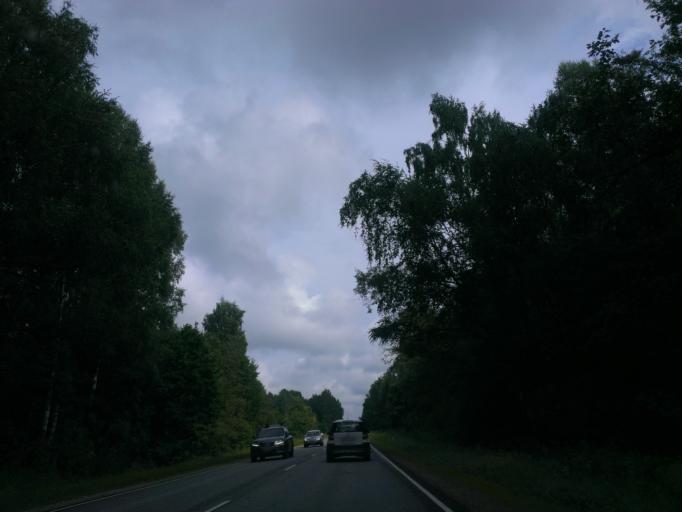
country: LV
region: Ligatne
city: Ligatne
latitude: 57.1821
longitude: 25.0091
